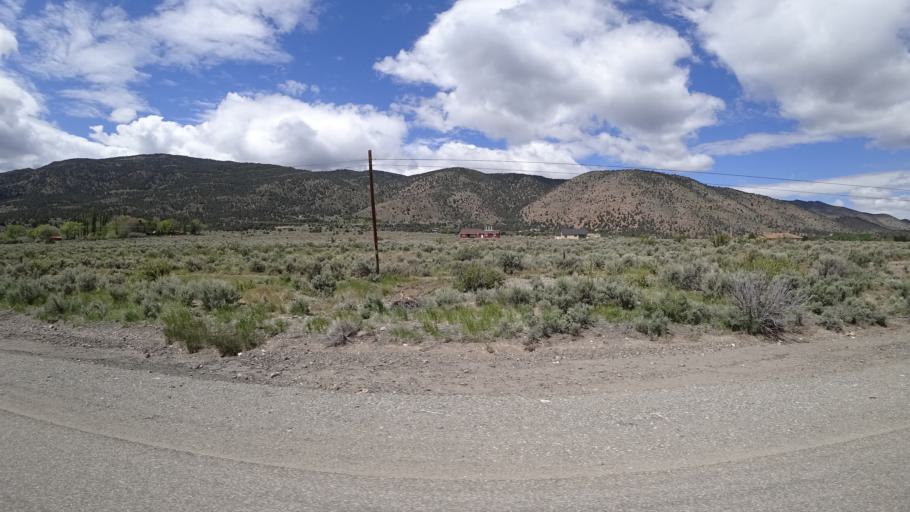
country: US
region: Nevada
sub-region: Lyon County
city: Smith Valley
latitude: 38.7268
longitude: -119.5551
